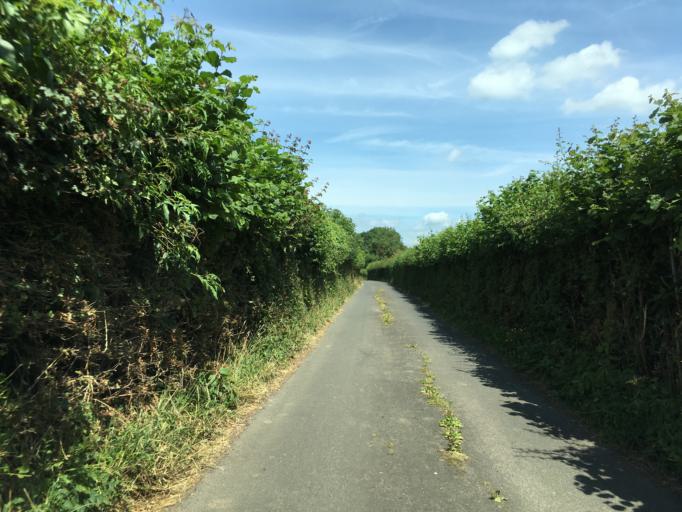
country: GB
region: Wales
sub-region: Newport
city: Llanwern
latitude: 51.5963
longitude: -2.9114
